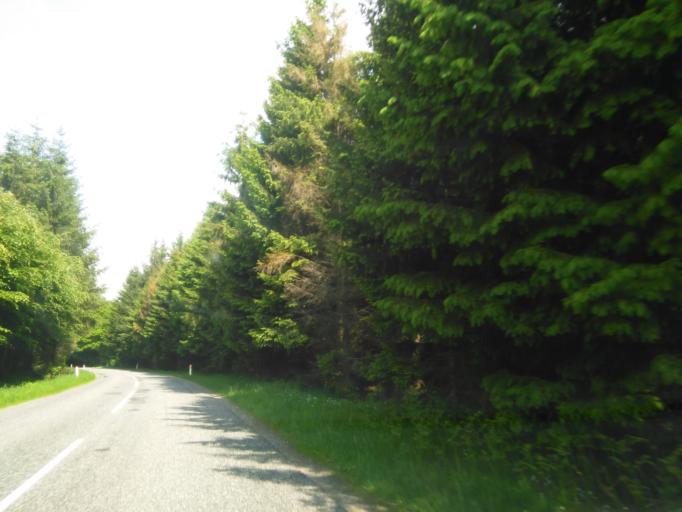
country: DK
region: Central Jutland
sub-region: Favrskov Kommune
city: Hammel
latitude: 56.2459
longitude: 9.9272
